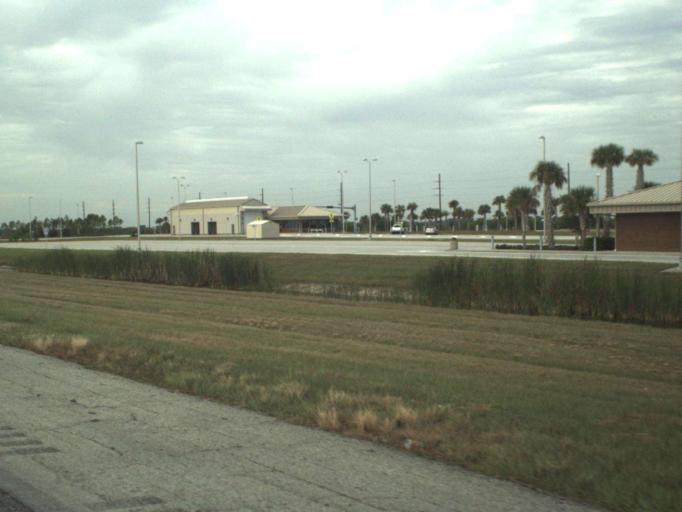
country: US
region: Florida
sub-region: Saint Lucie County
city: Port Saint Lucie
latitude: 27.1904
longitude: -80.3999
